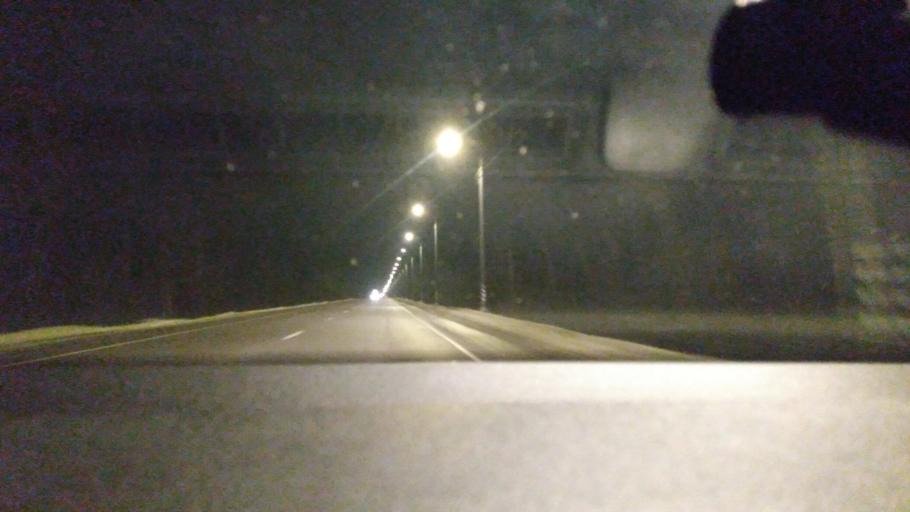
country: RU
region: Moskovskaya
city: Yegor'yevsk
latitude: 55.4507
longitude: 39.0041
